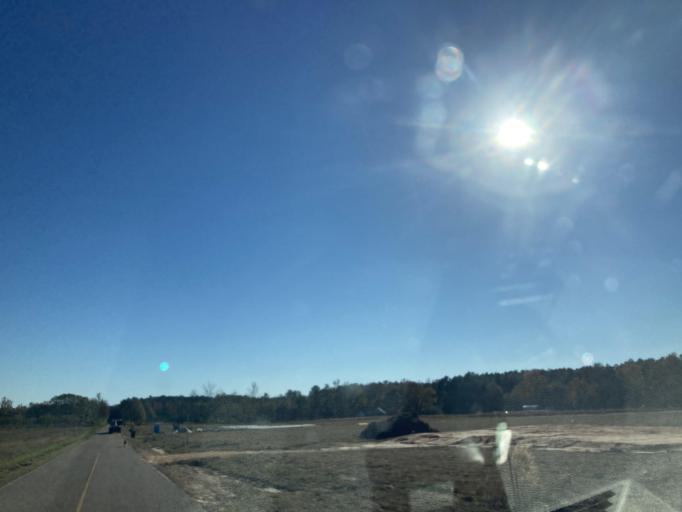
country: US
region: Mississippi
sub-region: Lamar County
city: Sumrall
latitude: 31.3875
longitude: -89.6075
